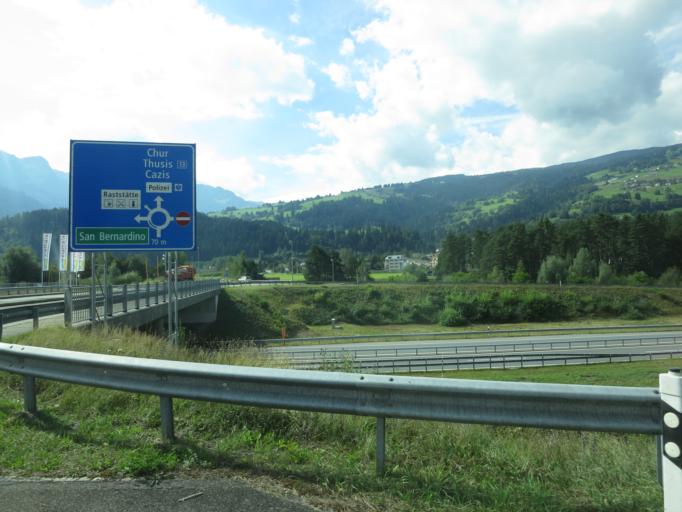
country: CH
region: Grisons
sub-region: Hinterrhein District
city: Thusis
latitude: 46.7147
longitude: 9.4458
